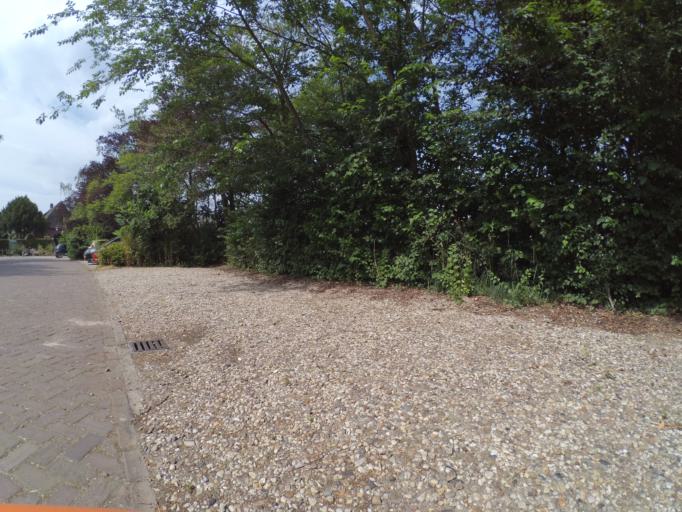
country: NL
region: Overijssel
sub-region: Gemeente Hof van Twente
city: Diepenheim
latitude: 52.1756
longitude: 6.5163
